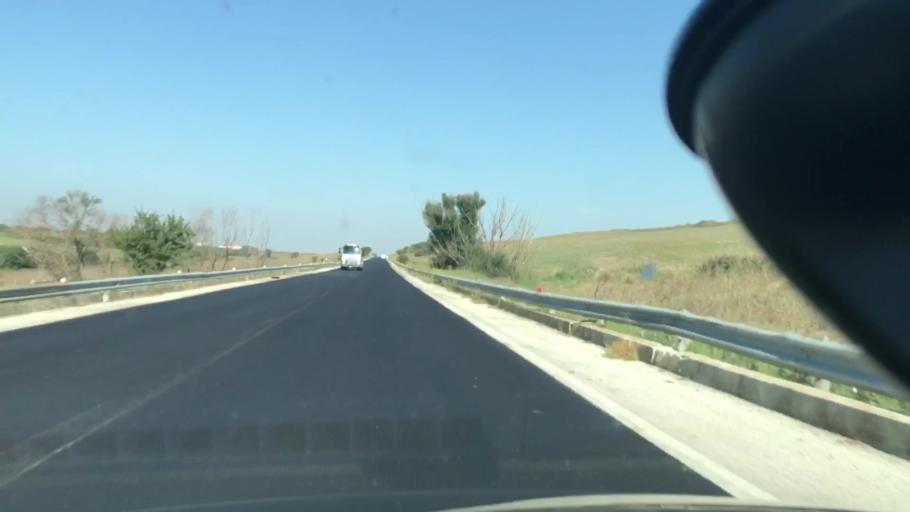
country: IT
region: Apulia
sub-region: Provincia di Barletta - Andria - Trani
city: Spinazzola
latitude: 40.9024
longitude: 16.1183
